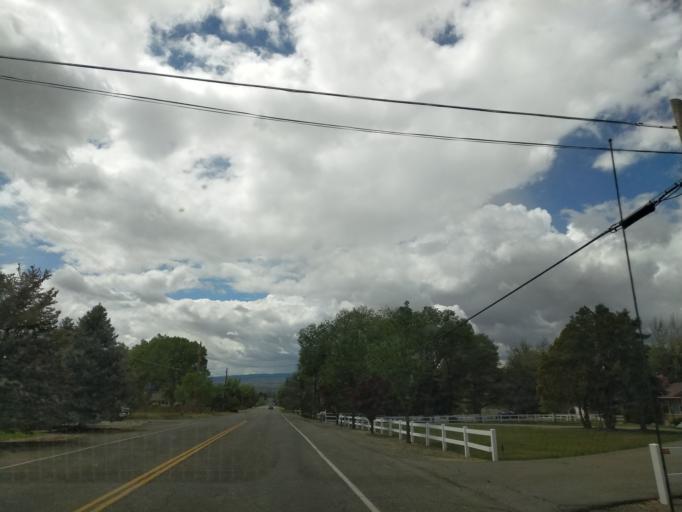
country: US
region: Colorado
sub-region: Mesa County
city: Grand Junction
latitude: 39.1040
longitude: -108.5618
